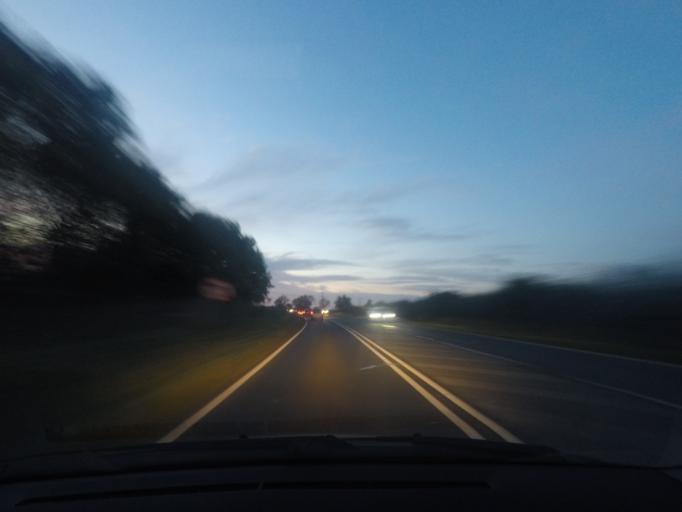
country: GB
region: England
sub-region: East Riding of Yorkshire
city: Wilberfoss
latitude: 53.9422
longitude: -0.8659
